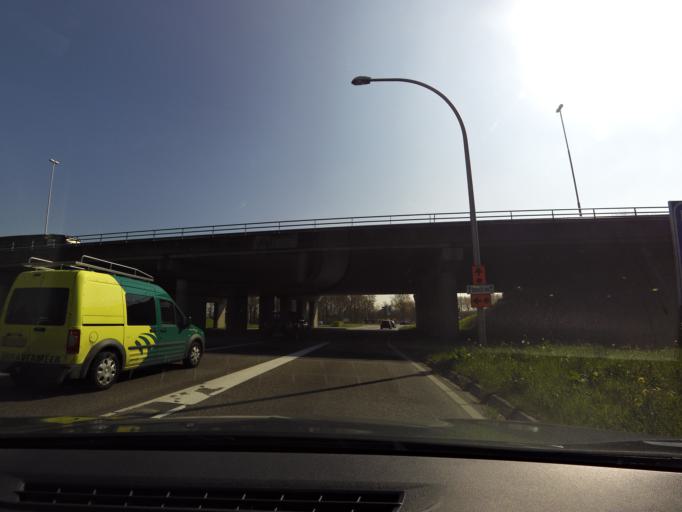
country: NL
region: South Holland
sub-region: Gemeente Maassluis
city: Maassluis
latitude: 51.9247
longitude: 4.2711
